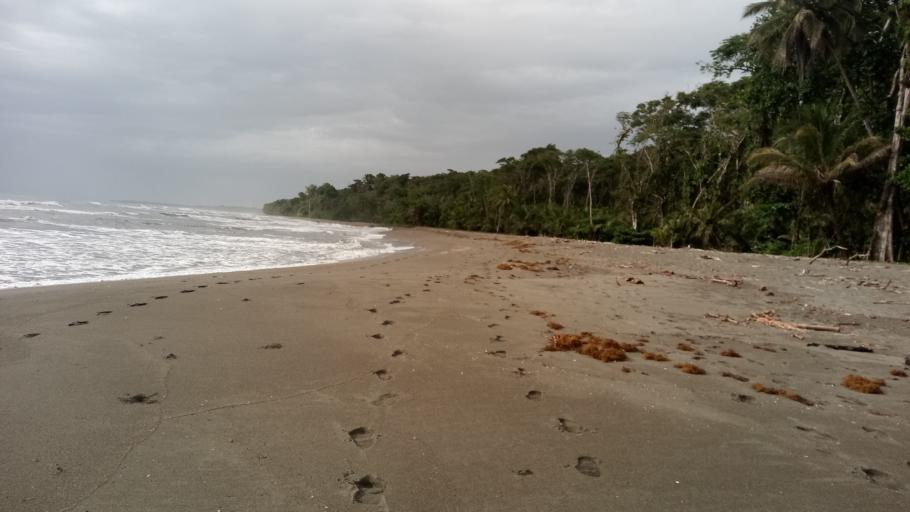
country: CR
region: Limon
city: Sixaola
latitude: 9.6150
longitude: -82.6200
